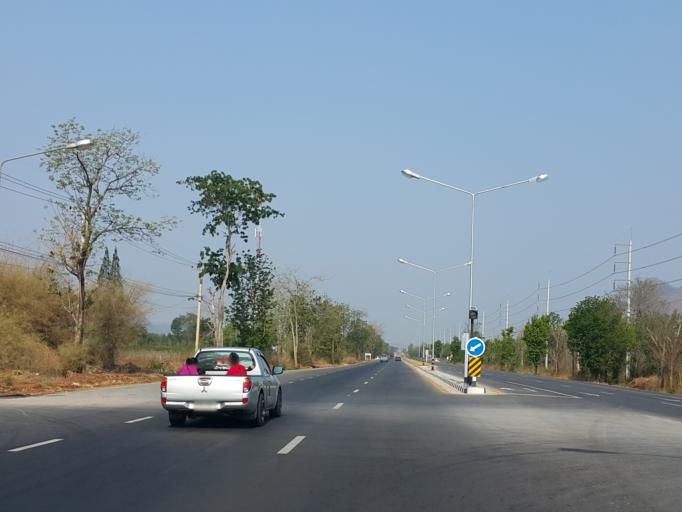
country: TH
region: Kanchanaburi
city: Kanchanaburi
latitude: 14.0874
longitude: 99.3772
